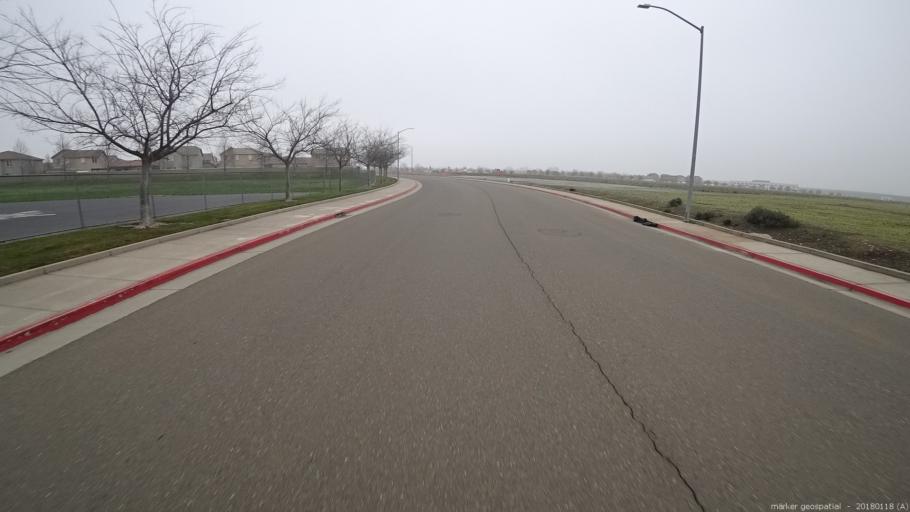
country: US
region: California
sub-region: Sacramento County
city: Rancho Cordova
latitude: 38.5726
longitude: -121.2839
